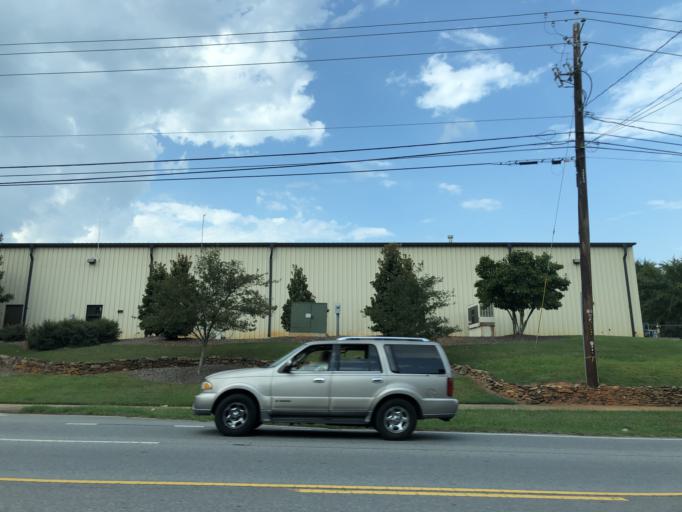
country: US
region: Georgia
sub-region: Clarke County
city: Athens
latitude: 33.9438
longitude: -83.3350
